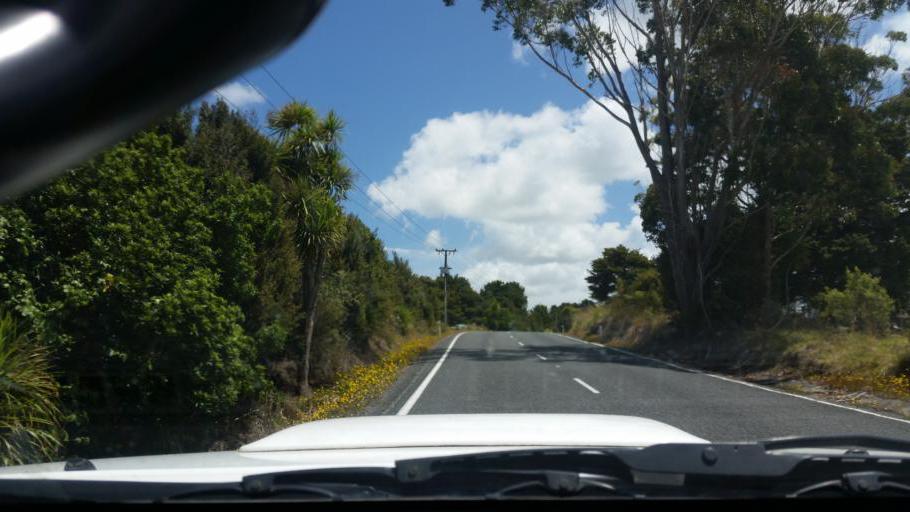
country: NZ
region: Northland
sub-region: Whangarei
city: Ruakaka
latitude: -36.0640
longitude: 174.2691
